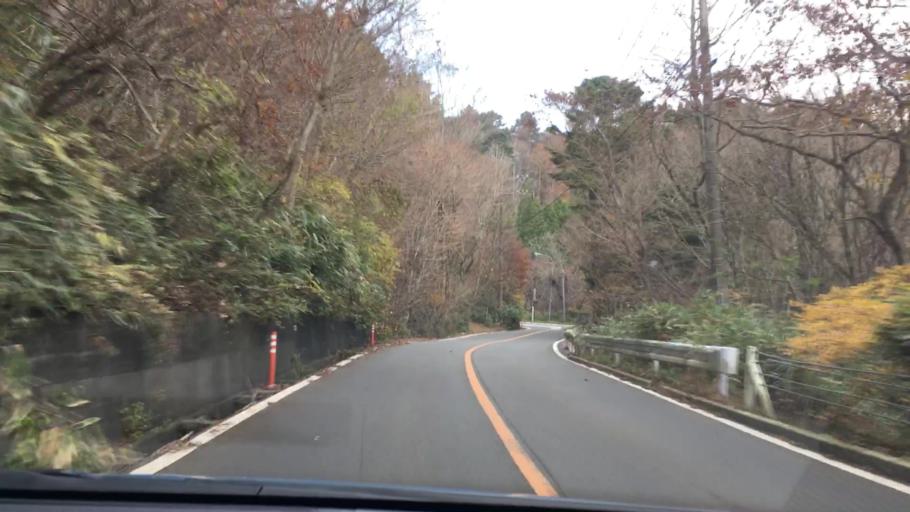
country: JP
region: Shizuoka
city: Gotemba
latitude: 35.4499
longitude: 138.9297
